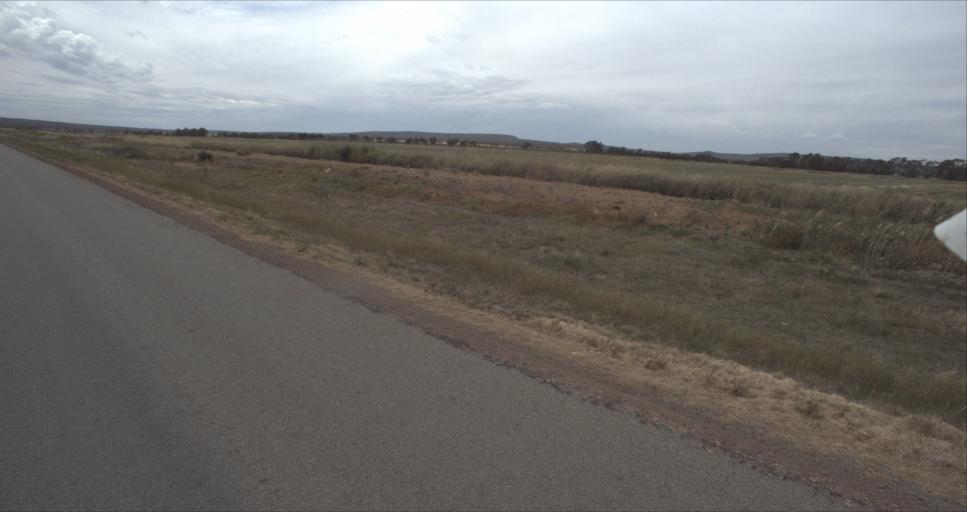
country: AU
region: New South Wales
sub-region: Leeton
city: Leeton
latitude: -34.5004
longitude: 146.3998
